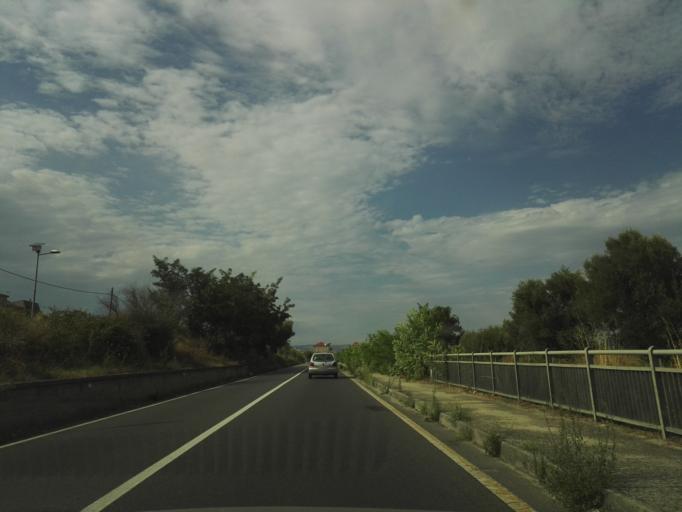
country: IT
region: Calabria
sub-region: Provincia di Catanzaro
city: Marina di Davoli
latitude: 38.6479
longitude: 16.5483
